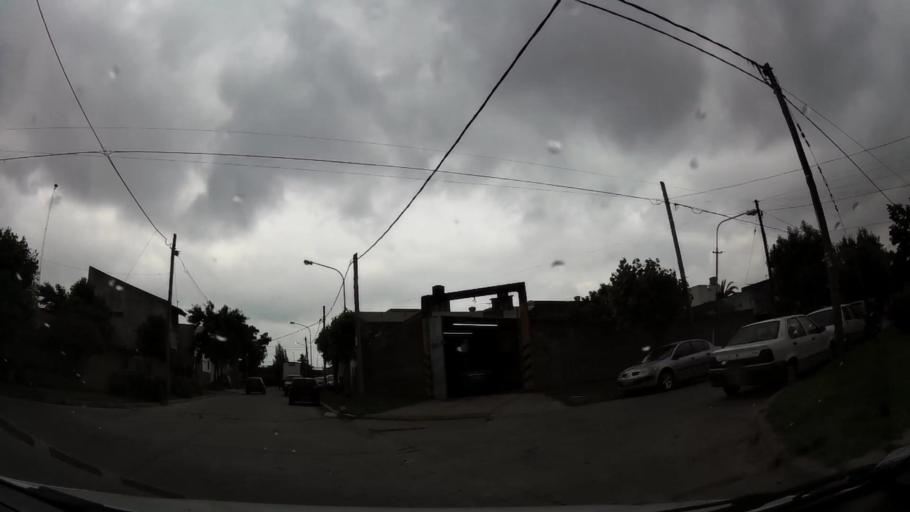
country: AR
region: Buenos Aires
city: San Justo
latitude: -34.7100
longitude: -58.5263
